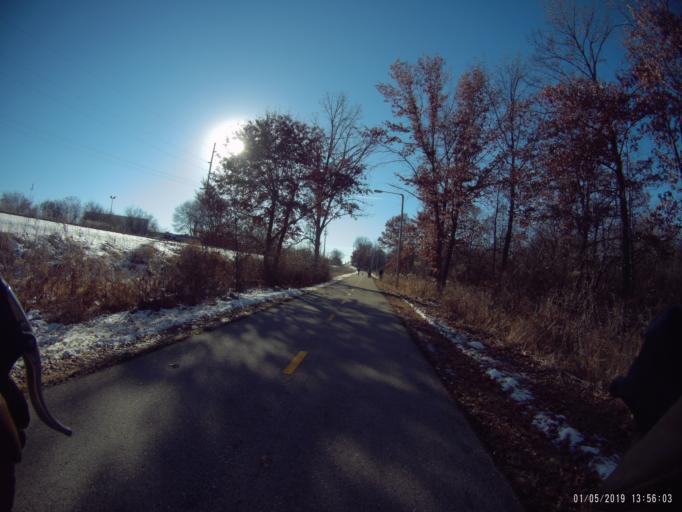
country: US
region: Wisconsin
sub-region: Dane County
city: Madison
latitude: 43.0383
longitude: -89.4106
